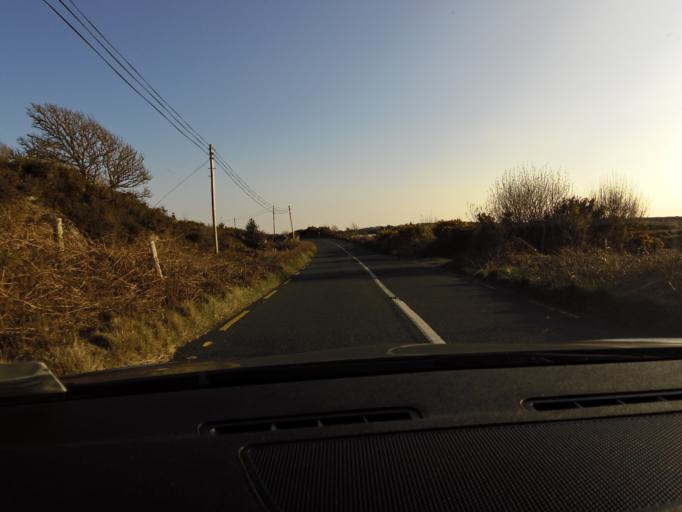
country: IE
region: Connaught
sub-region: County Galway
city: Oughterard
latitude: 53.3054
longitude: -9.5556
